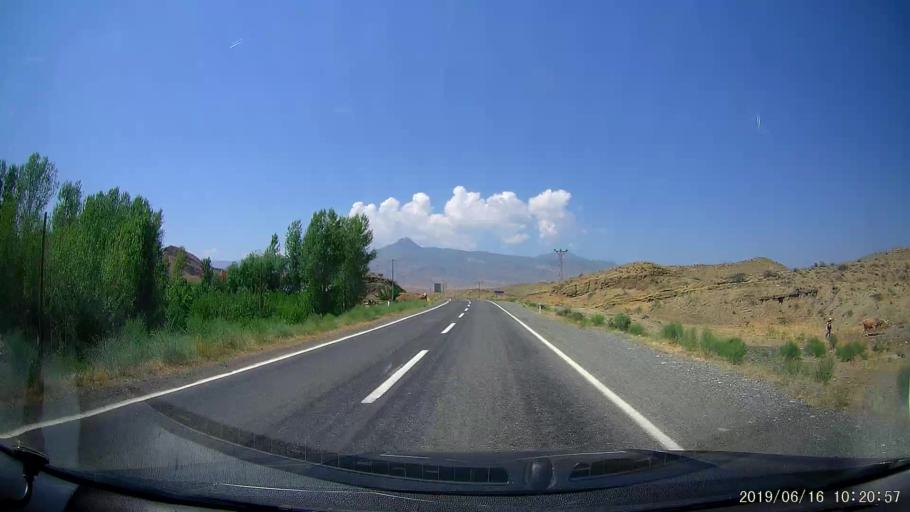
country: TR
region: Igdir
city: Tuzluca
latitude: 40.1427
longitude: 43.6421
